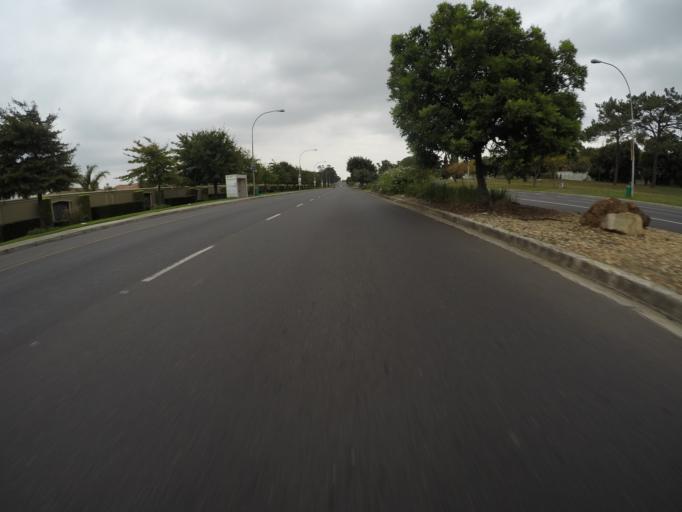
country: ZA
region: Western Cape
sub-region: City of Cape Town
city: Kraaifontein
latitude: -33.8478
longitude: 18.6444
